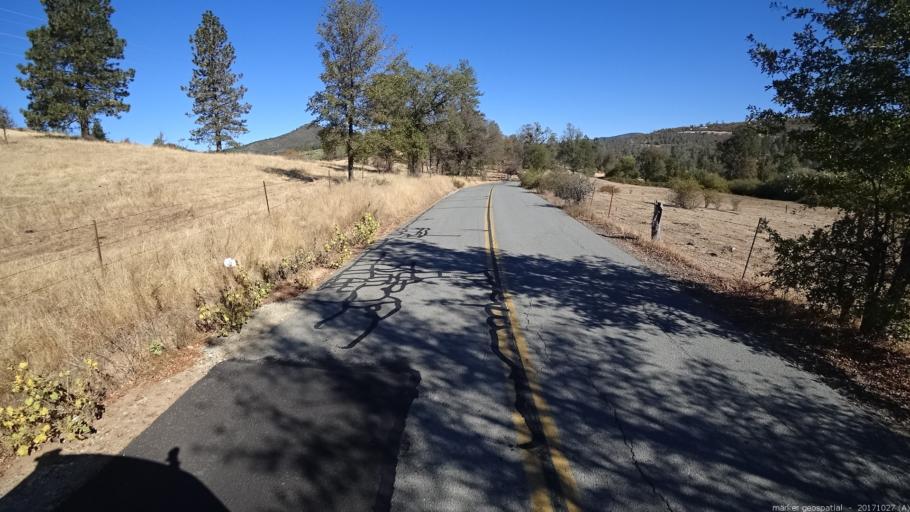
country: US
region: California
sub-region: Shasta County
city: Shingletown
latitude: 40.7717
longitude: -121.9657
